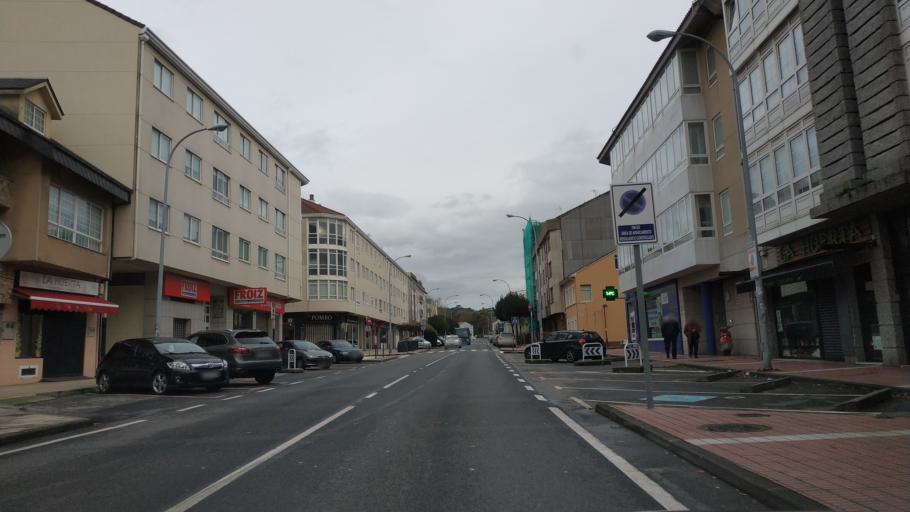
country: ES
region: Galicia
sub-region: Provincia da Coruna
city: Oleiros
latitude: 43.3492
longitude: -8.3453
